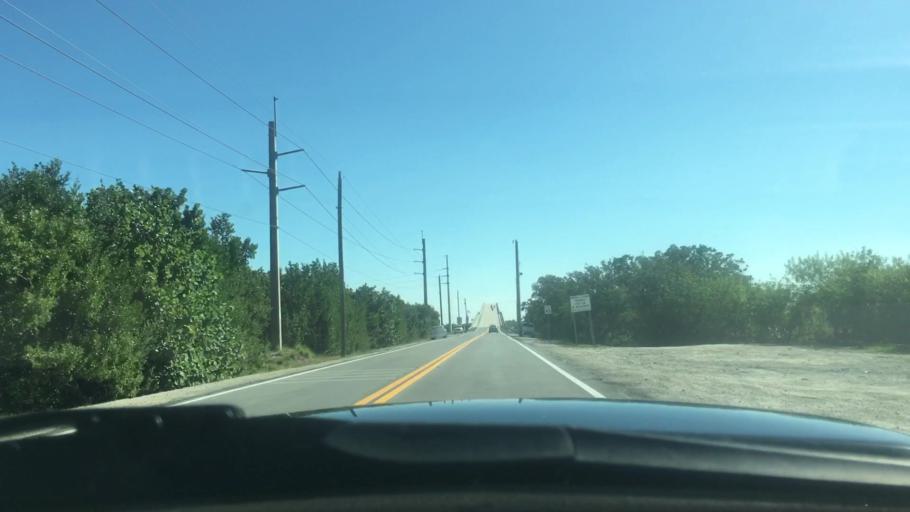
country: US
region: Florida
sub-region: Monroe County
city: North Key Largo
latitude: 25.2900
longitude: -80.3751
